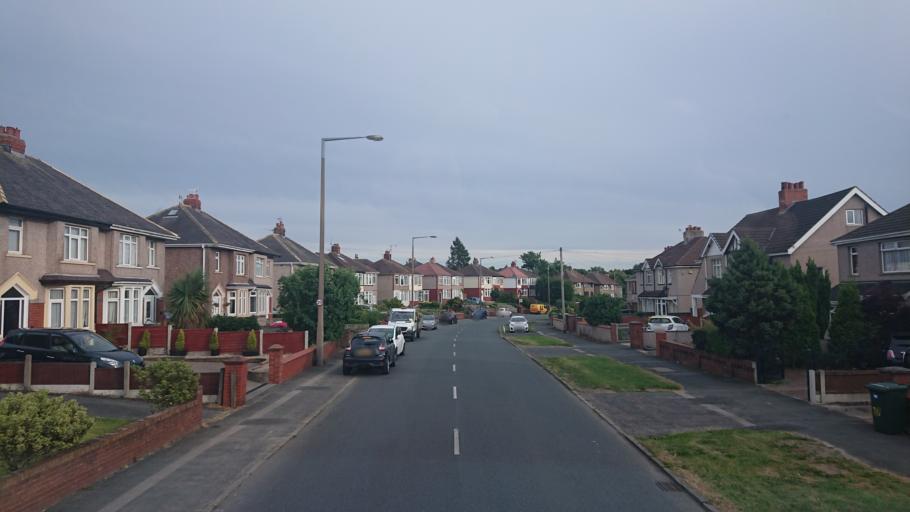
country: GB
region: England
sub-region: Lancashire
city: Lancaster
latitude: 54.0584
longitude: -2.8167
